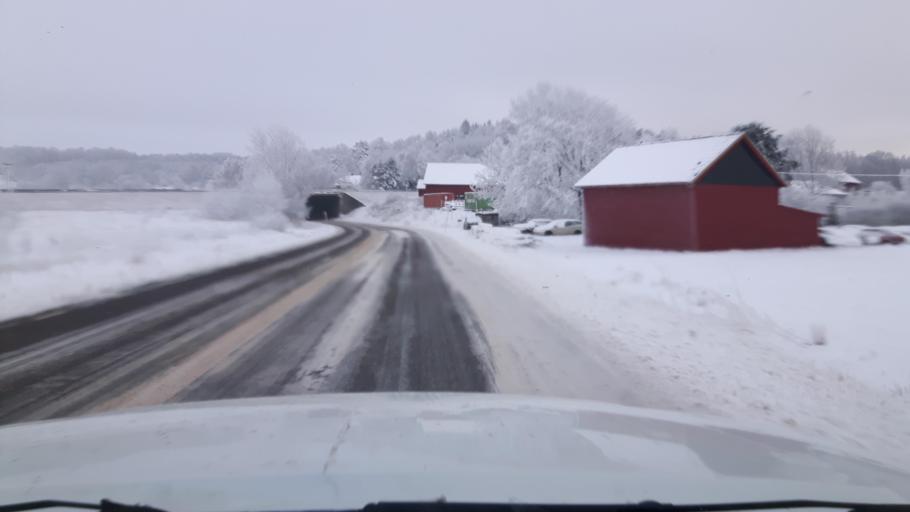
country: SE
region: Halland
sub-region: Kungsbacka Kommun
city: Kungsbacka
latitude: 57.4520
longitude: 12.0913
